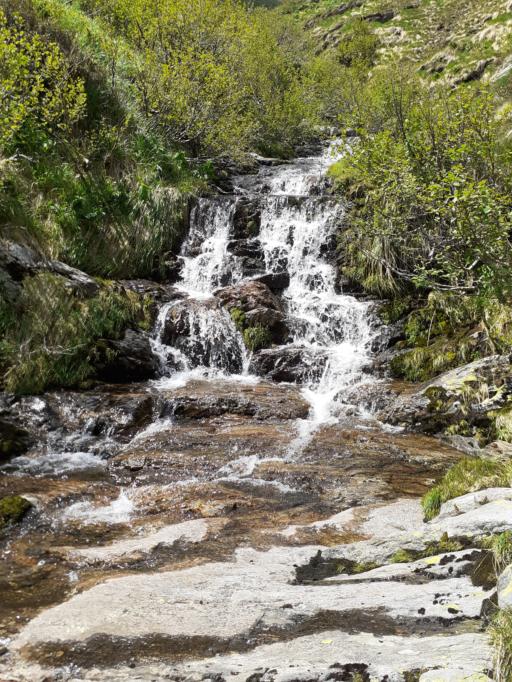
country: IT
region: Piedmont
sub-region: Provincia Verbano-Cusio-Ossola
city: Santa Maria Maggiore
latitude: 46.0697
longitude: 8.4531
